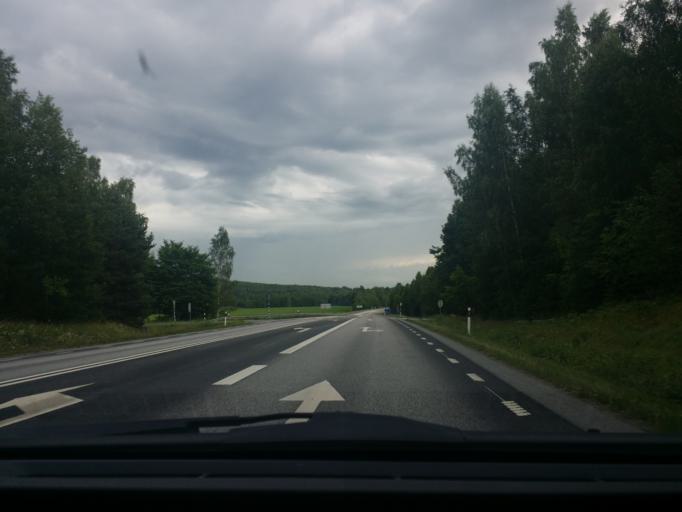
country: SE
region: OErebro
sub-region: Nora Kommun
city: Nora
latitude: 59.4937
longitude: 15.0506
